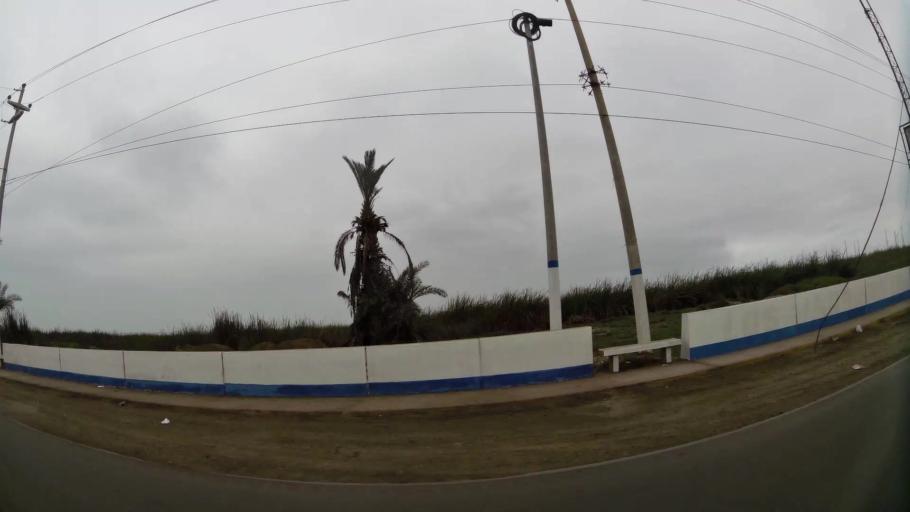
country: PE
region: Ica
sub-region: Provincia de Pisco
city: Pisco
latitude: -13.7192
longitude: -76.2203
